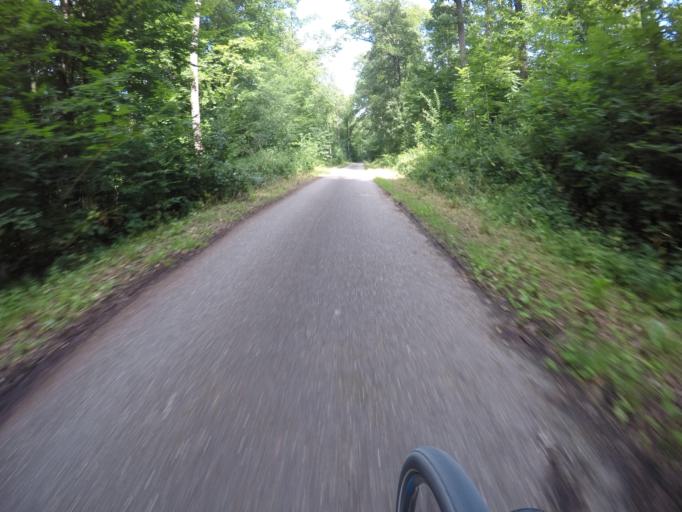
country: DE
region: Baden-Wuerttemberg
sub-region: Karlsruhe Region
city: Otisheim
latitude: 48.9823
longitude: 8.7839
